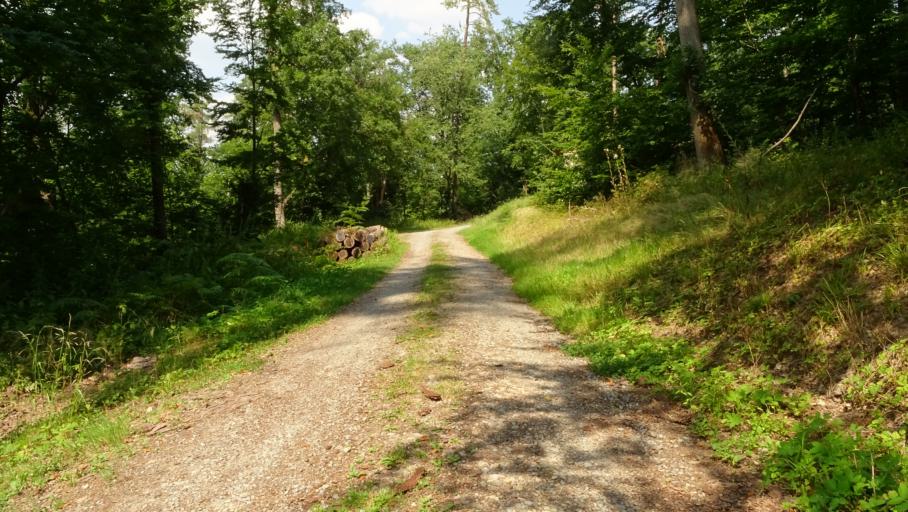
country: DE
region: Baden-Wuerttemberg
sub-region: Karlsruhe Region
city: Neckargerach
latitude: 49.4004
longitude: 9.0807
